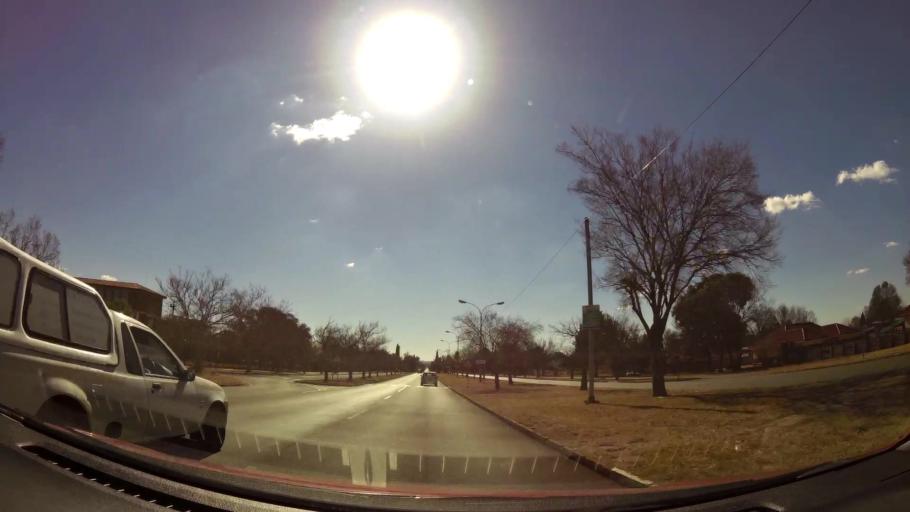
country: ZA
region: Gauteng
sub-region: West Rand District Municipality
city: Carletonville
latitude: -26.3685
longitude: 27.4042
